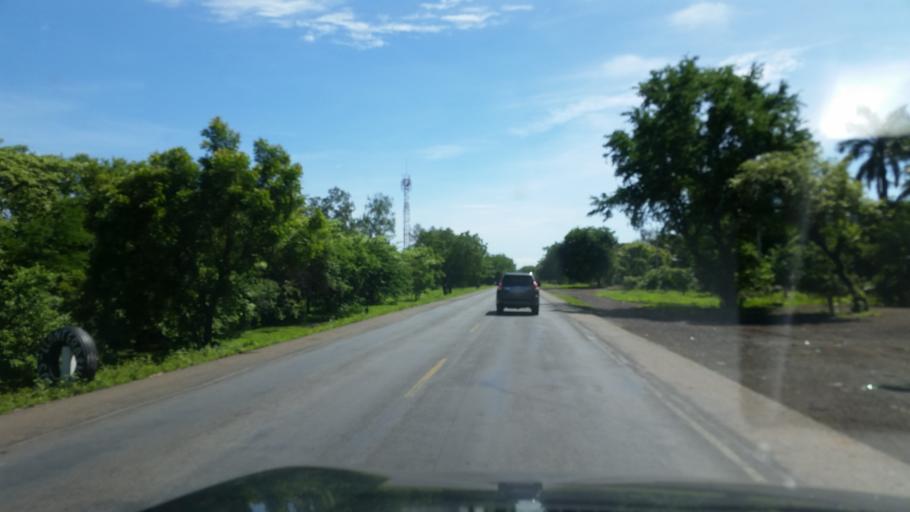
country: NI
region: Chinandega
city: Puerto Morazan
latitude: 12.7635
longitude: -87.0604
